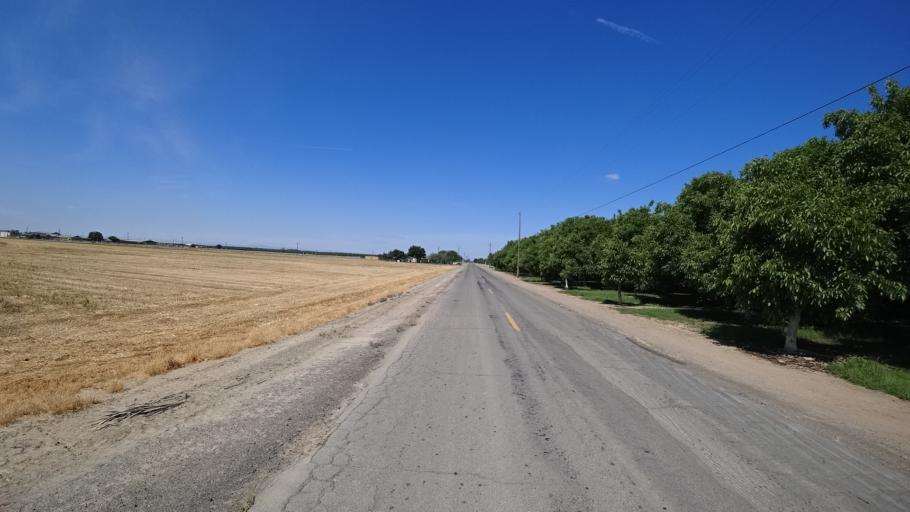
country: US
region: California
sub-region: Kings County
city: Armona
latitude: 36.2693
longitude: -119.6794
